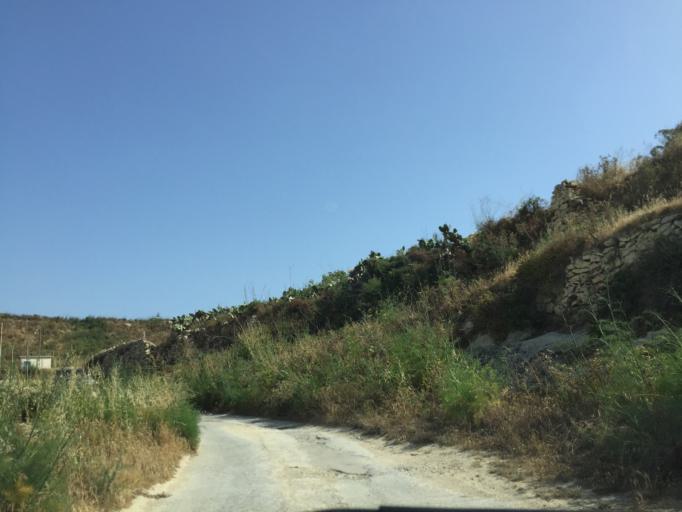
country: MT
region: L-Gharb
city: Gharb
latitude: 36.0673
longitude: 14.2056
